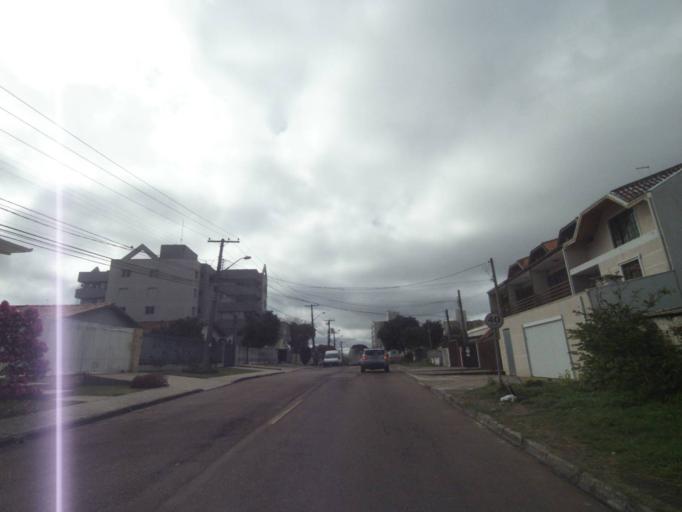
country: BR
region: Parana
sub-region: Curitiba
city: Curitiba
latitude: -25.4982
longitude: -49.2928
